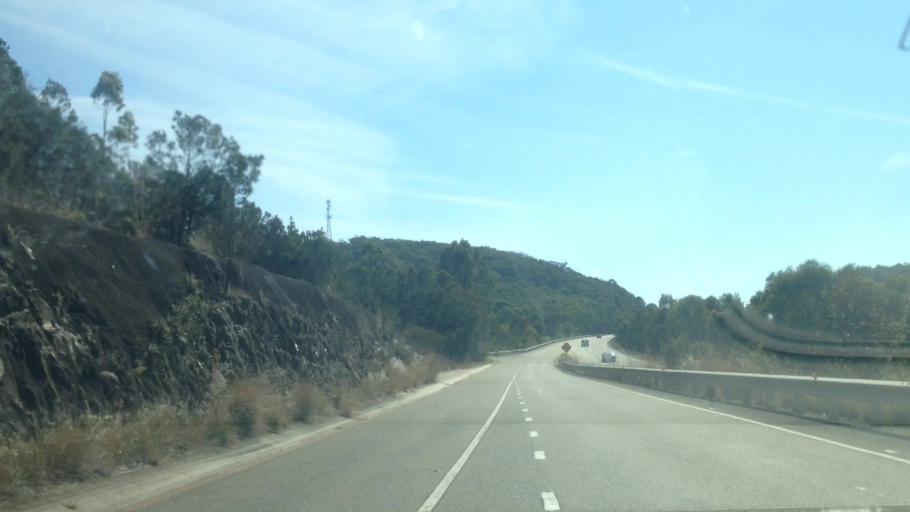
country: AU
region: New South Wales
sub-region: Lake Macquarie Shire
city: Toronto
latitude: -32.9859
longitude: 151.5197
